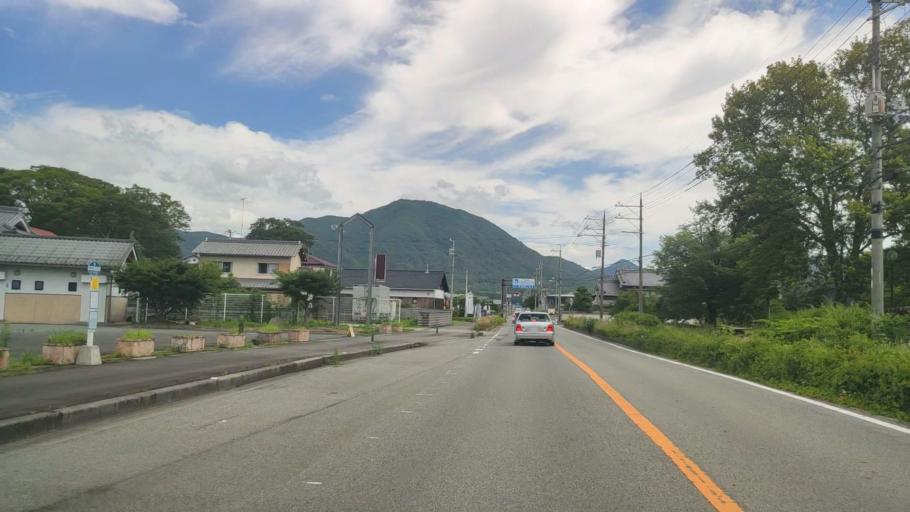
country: JP
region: Hyogo
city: Nishiwaki
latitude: 35.0581
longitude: 134.9190
